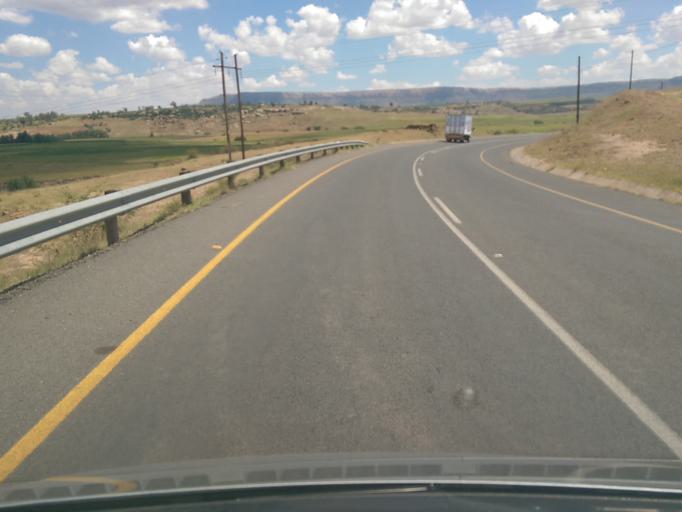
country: LS
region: Maseru
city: Maseru
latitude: -29.3918
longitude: 27.5475
